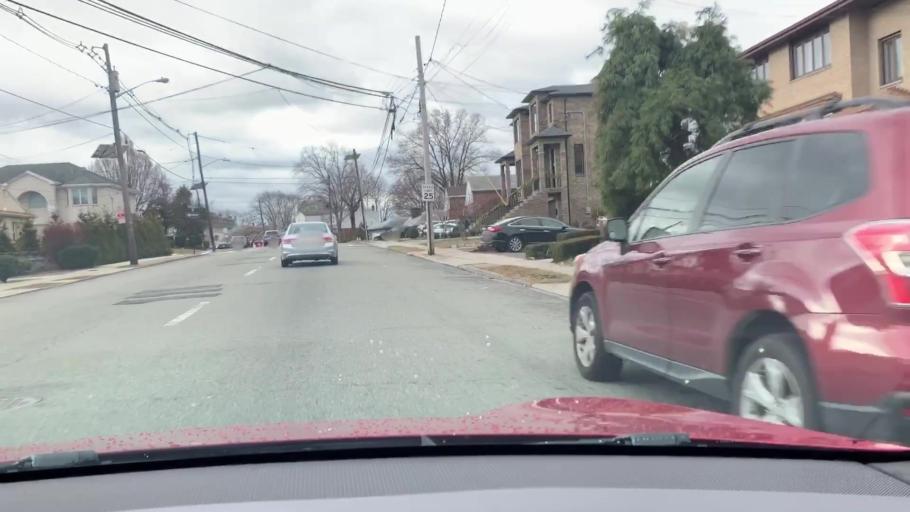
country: US
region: New Jersey
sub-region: Bergen County
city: Fort Lee
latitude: 40.8502
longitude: -73.9775
